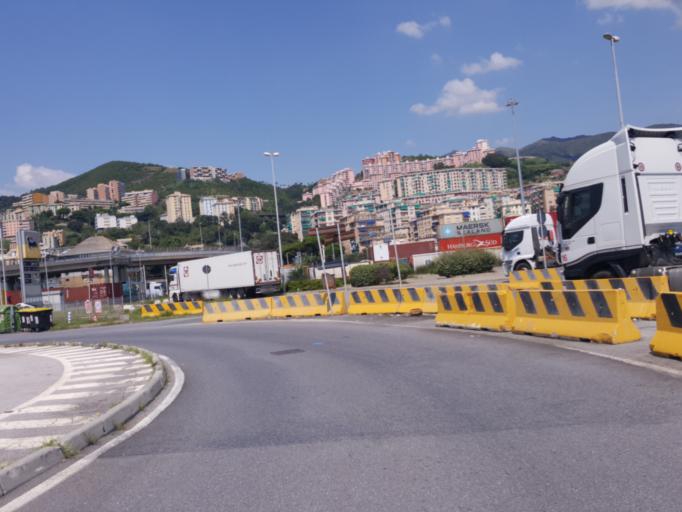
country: IT
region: Liguria
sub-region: Provincia di Genova
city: Mele
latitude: 44.4257
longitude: 8.7695
